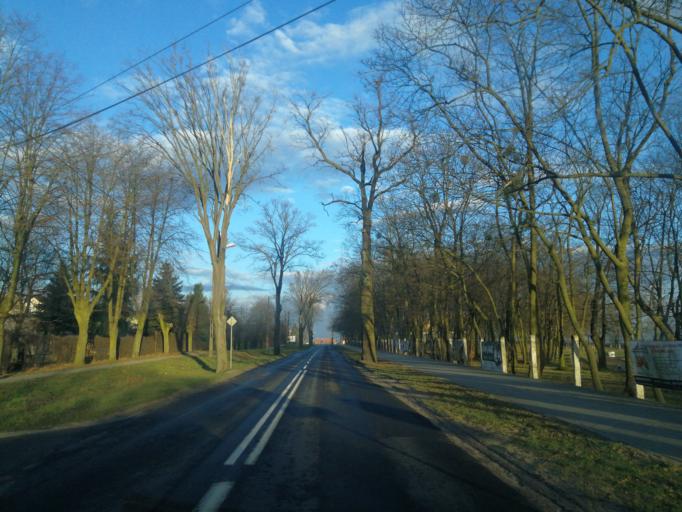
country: PL
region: Kujawsko-Pomorskie
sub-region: Powiat torunski
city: Chelmza
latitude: 53.1885
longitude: 18.6246
